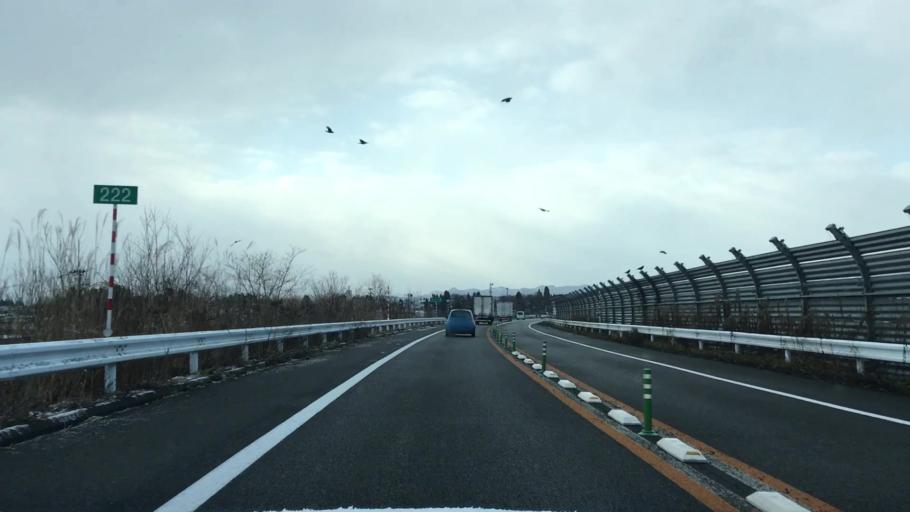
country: JP
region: Akita
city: Odate
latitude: 40.2839
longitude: 140.5406
